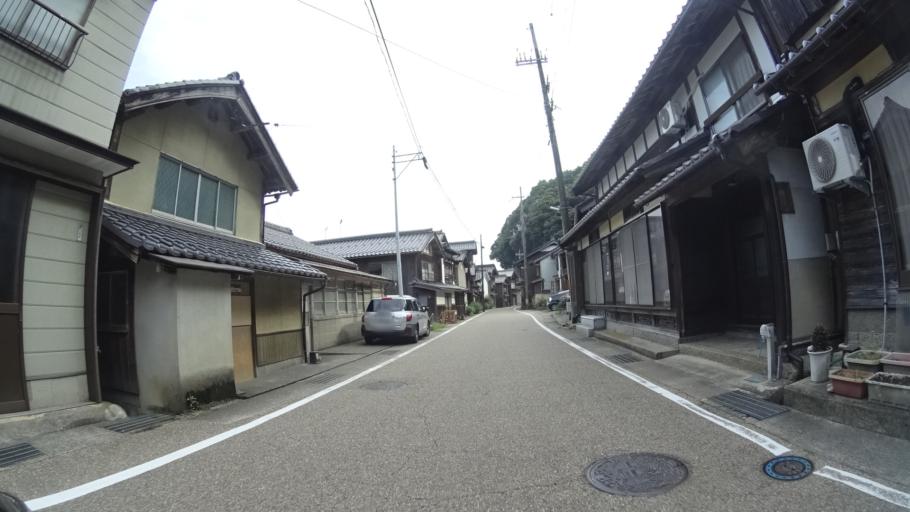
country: JP
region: Kyoto
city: Miyazu
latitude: 35.6716
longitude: 135.2838
